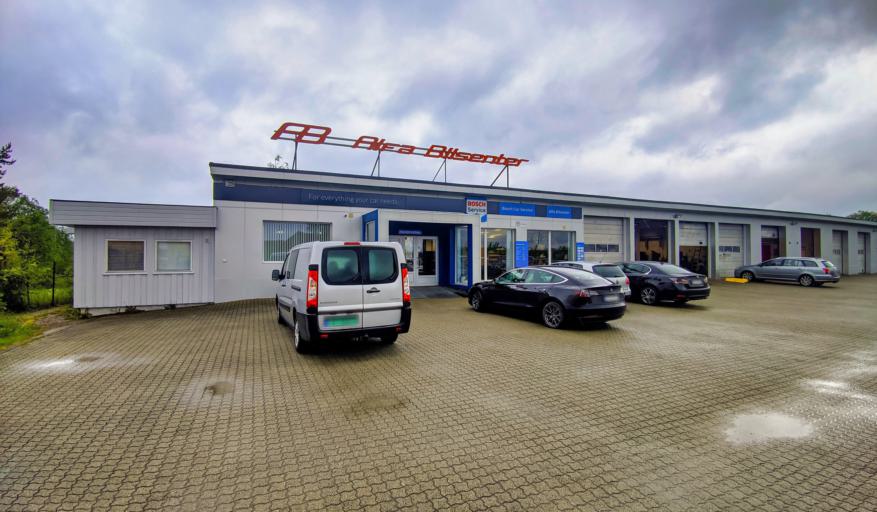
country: NO
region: Akershus
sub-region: Nes
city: Neskollen
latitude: 60.1344
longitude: 11.2879
